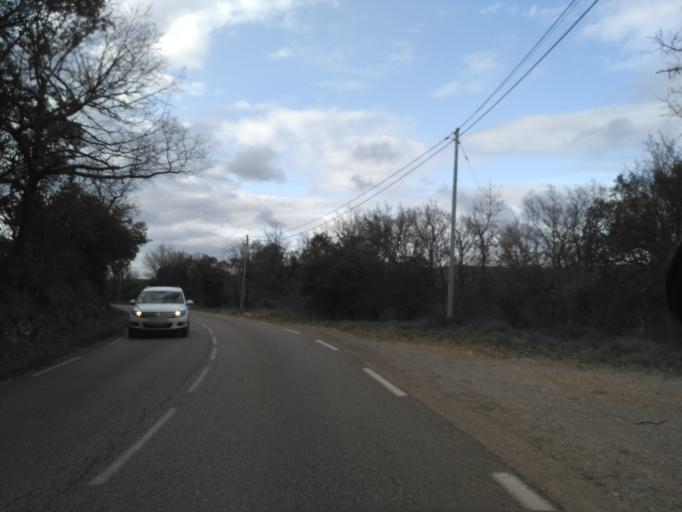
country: FR
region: Provence-Alpes-Cote d'Azur
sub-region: Departement du Var
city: Barjols
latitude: 43.5768
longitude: 6.0164
